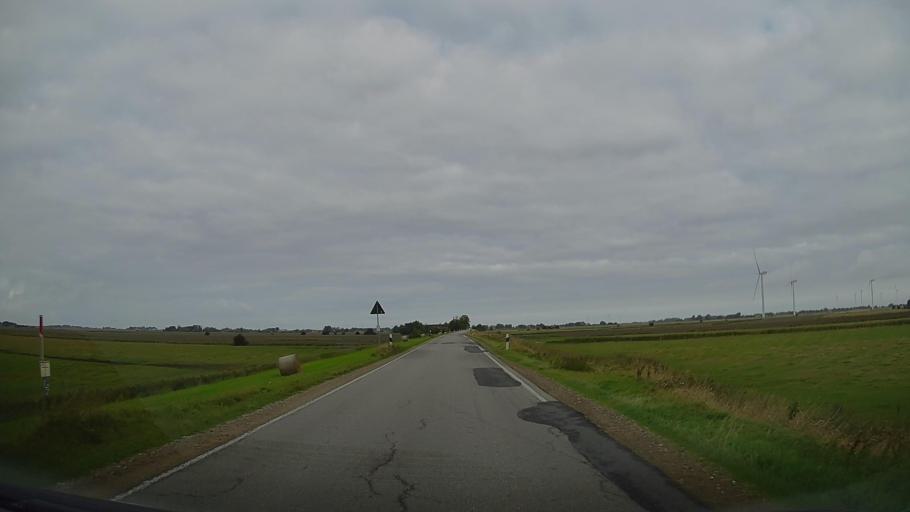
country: DE
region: Schleswig-Holstein
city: Galmsbull
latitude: 54.7866
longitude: 8.7317
